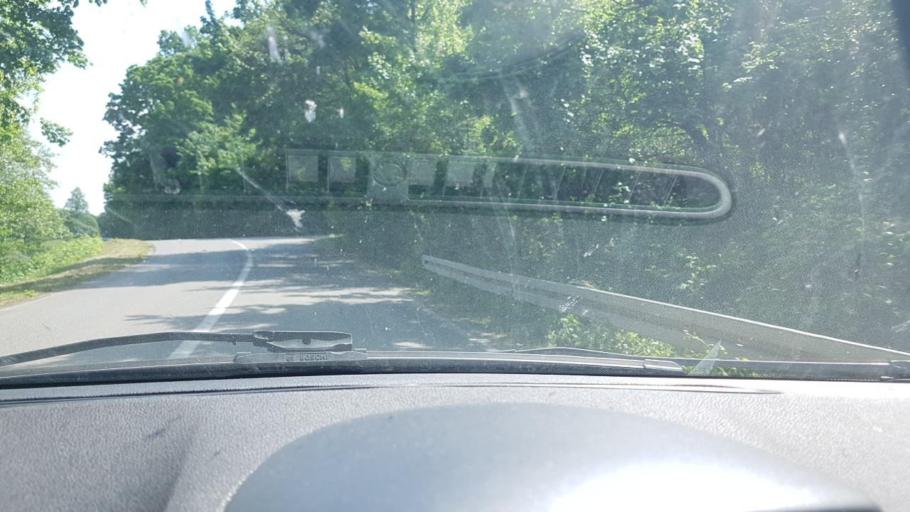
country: HR
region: Grad Zagreb
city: Dubrava
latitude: 45.8550
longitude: 16.0254
